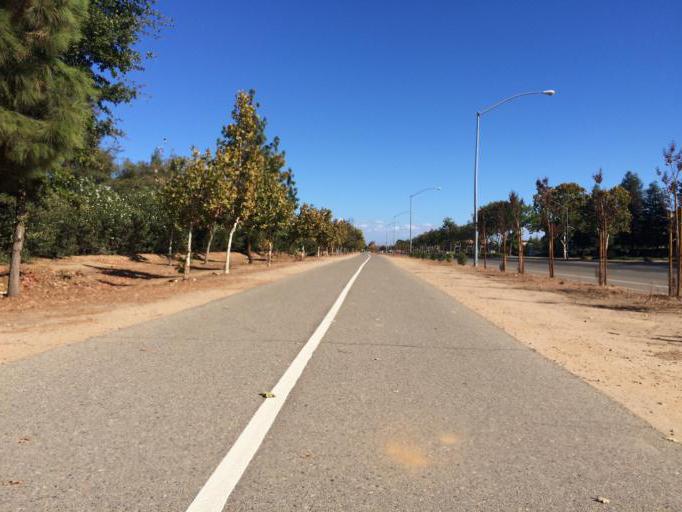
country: US
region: California
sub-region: Fresno County
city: Clovis
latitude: 36.8668
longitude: -119.7441
